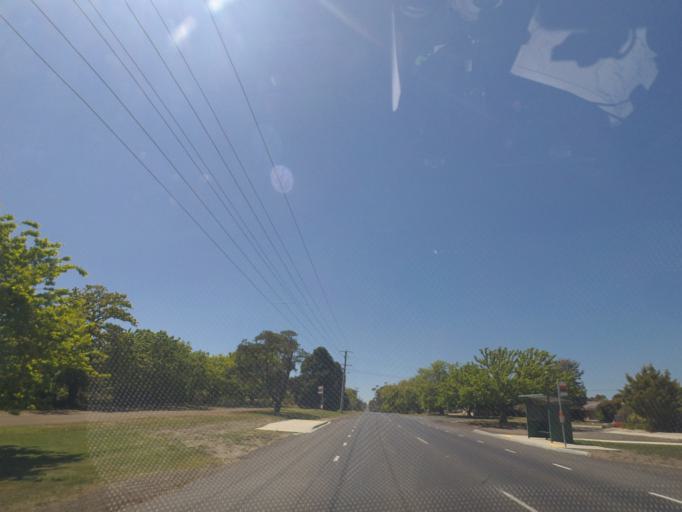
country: AU
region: Victoria
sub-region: Hume
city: Sunbury
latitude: -37.4574
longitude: 144.6834
